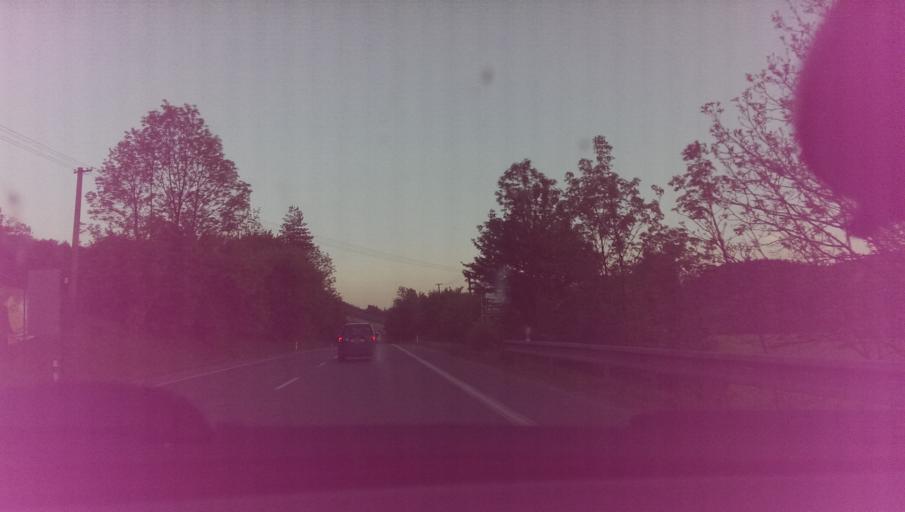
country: CZ
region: Zlin
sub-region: Okres Vsetin
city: Vsetin
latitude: 49.3222
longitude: 18.0032
